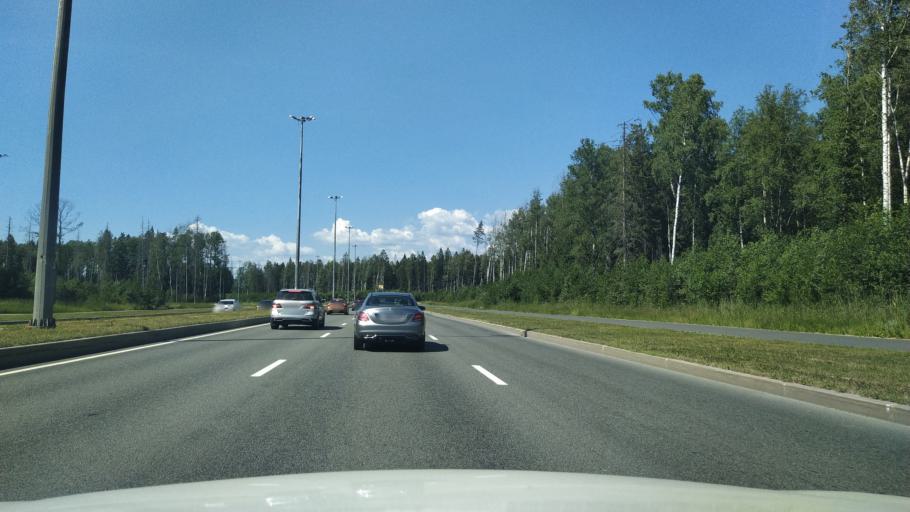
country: RU
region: St.-Petersburg
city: Levashovo
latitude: 60.0613
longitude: 30.2172
